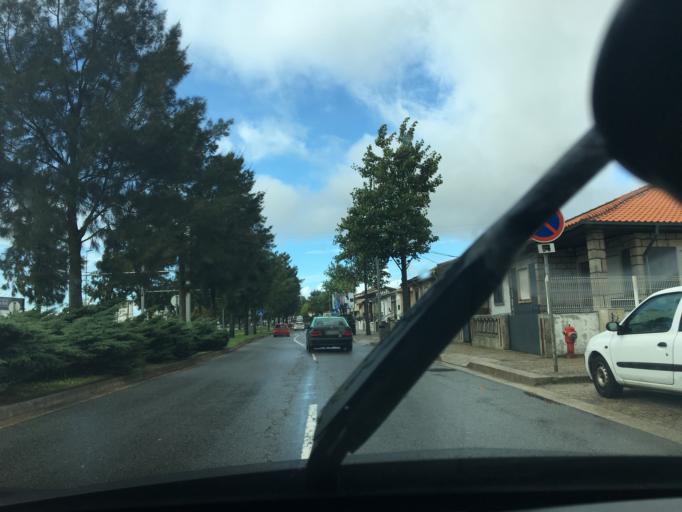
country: PT
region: Porto
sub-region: Matosinhos
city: Santa Cruz do Bispo
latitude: 41.2390
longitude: -8.6606
